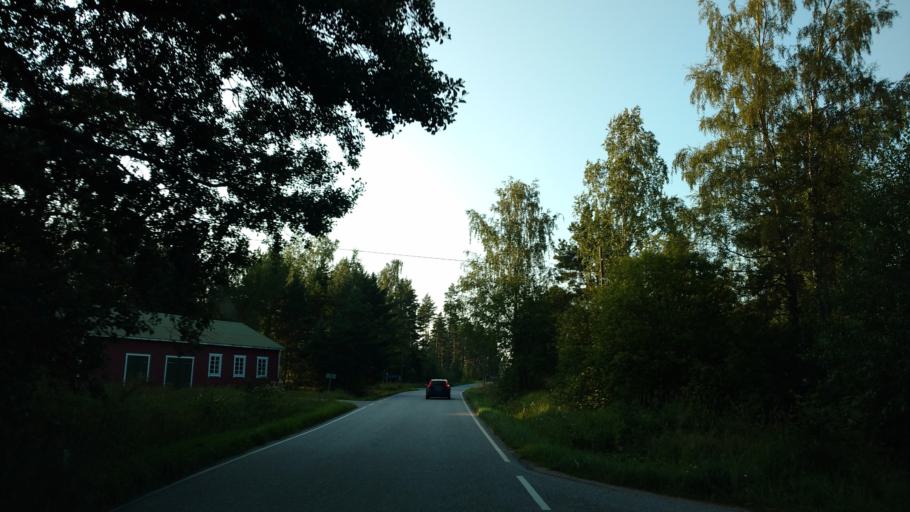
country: FI
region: Varsinais-Suomi
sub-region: Aboland-Turunmaa
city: Dragsfjaerd
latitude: 60.0646
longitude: 22.4515
